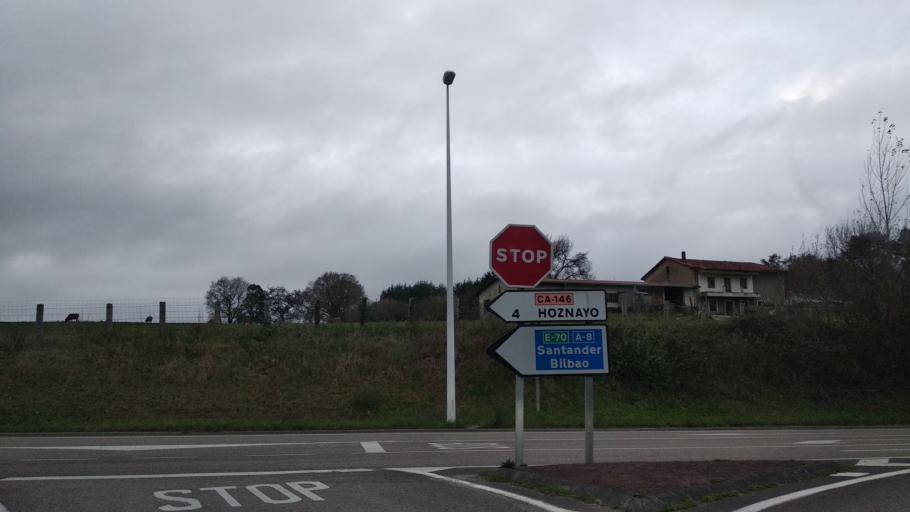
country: ES
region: Cantabria
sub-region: Provincia de Cantabria
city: Entrambasaguas
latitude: 43.4188
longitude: -3.7081
